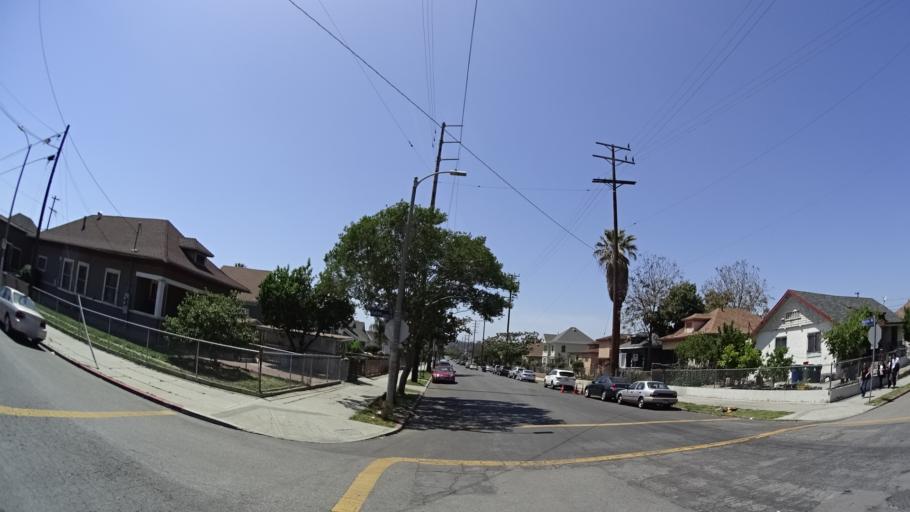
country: US
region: California
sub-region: Los Angeles County
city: Boyle Heights
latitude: 34.0719
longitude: -118.2065
